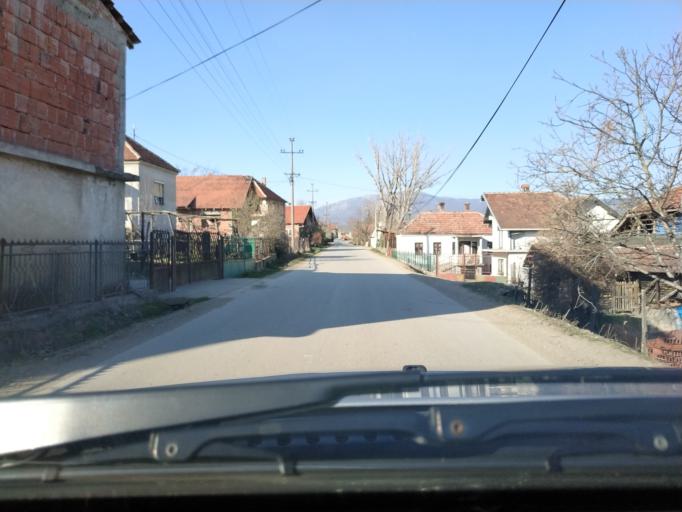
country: RS
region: Central Serbia
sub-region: Nisavski Okrug
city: Aleksinac
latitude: 43.5079
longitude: 21.7968
